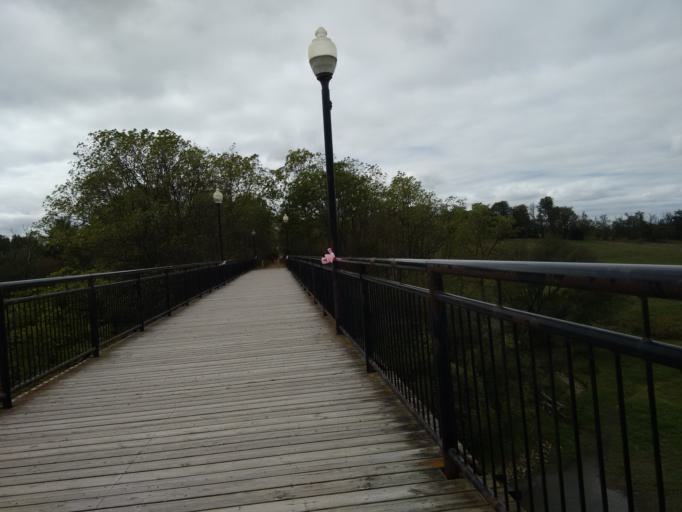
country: CA
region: Ontario
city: Stratford
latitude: 43.2634
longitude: -81.1483
